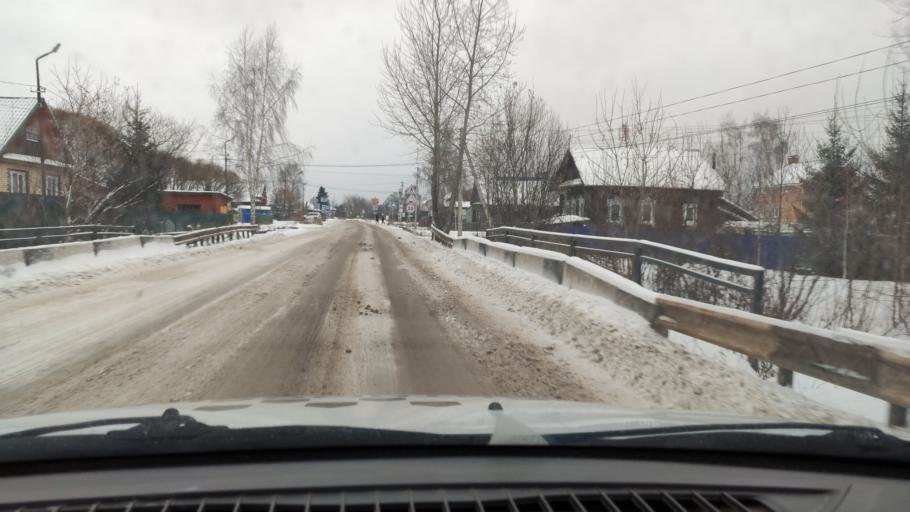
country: RU
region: Perm
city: Froly
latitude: 57.8852
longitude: 56.2575
